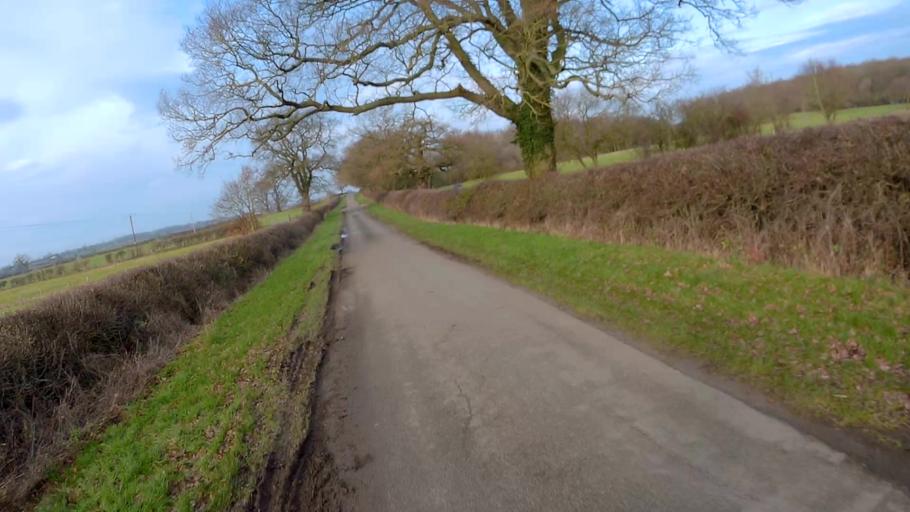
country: GB
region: England
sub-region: Lincolnshire
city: Bourne
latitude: 52.7638
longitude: -0.4201
